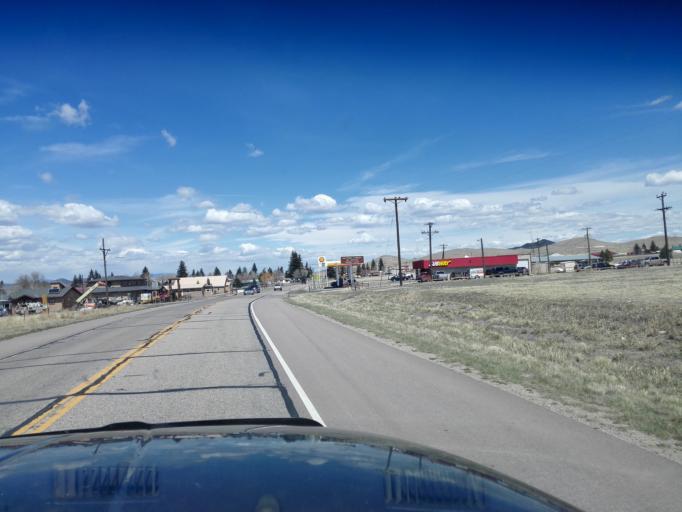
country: US
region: Colorado
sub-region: Custer County
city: Westcliffe
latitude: 38.1300
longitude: -105.4637
